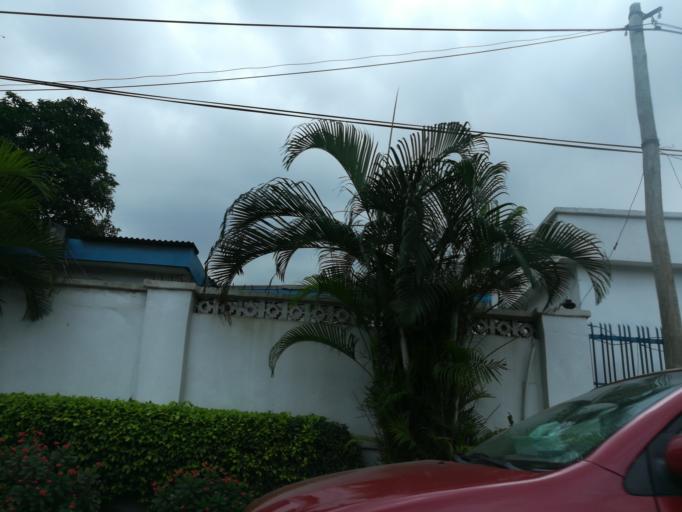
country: NG
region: Lagos
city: Ikeja
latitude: 6.6166
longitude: 3.3461
